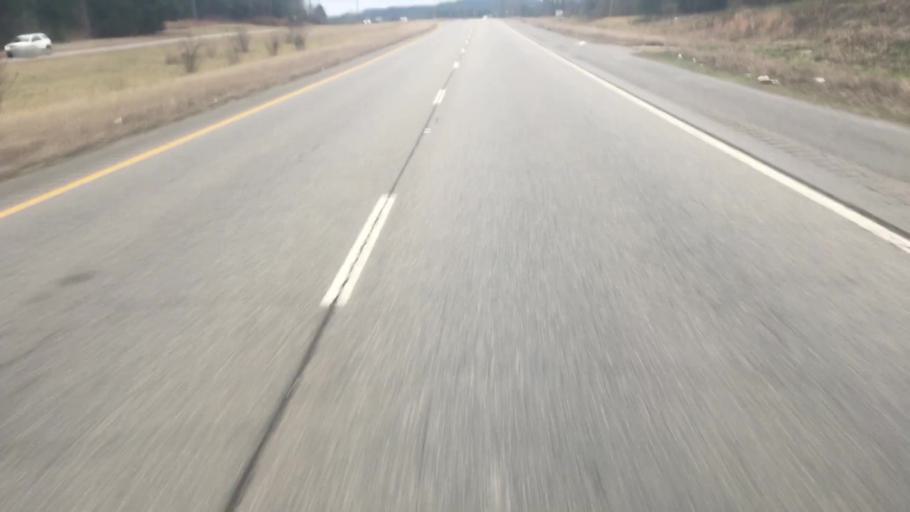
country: US
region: Alabama
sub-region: Walker County
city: Dora
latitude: 33.7985
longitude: -87.1132
